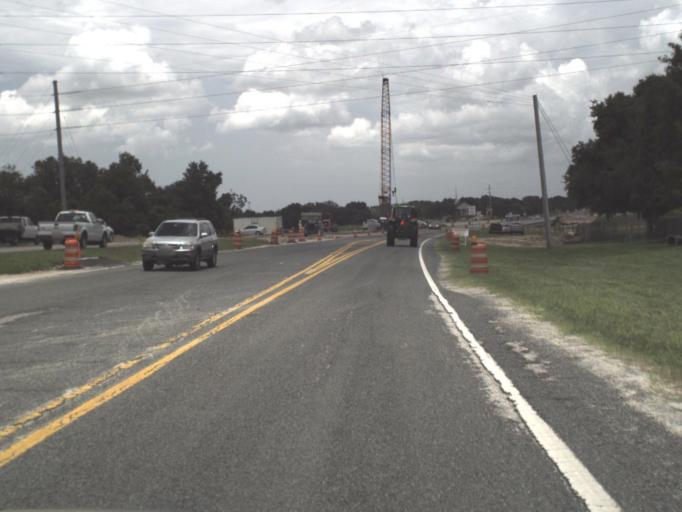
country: US
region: Florida
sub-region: Hillsborough County
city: Temple Terrace
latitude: 28.0430
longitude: -82.3473
